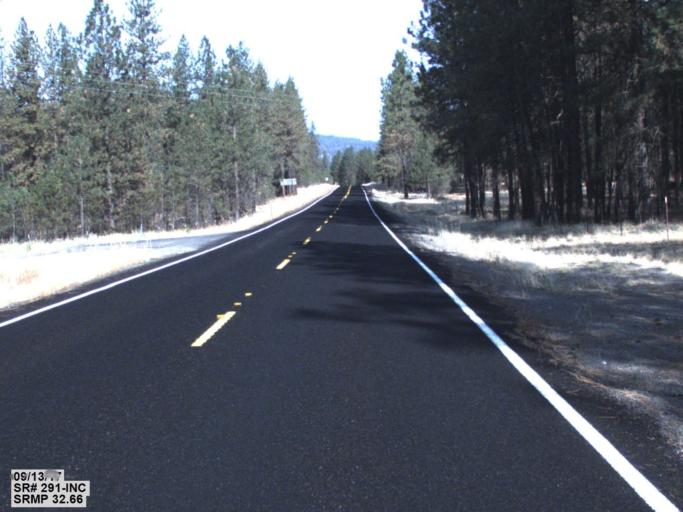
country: US
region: Washington
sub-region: Spokane County
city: Fairchild Air Force Base
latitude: 47.8444
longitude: -117.8486
